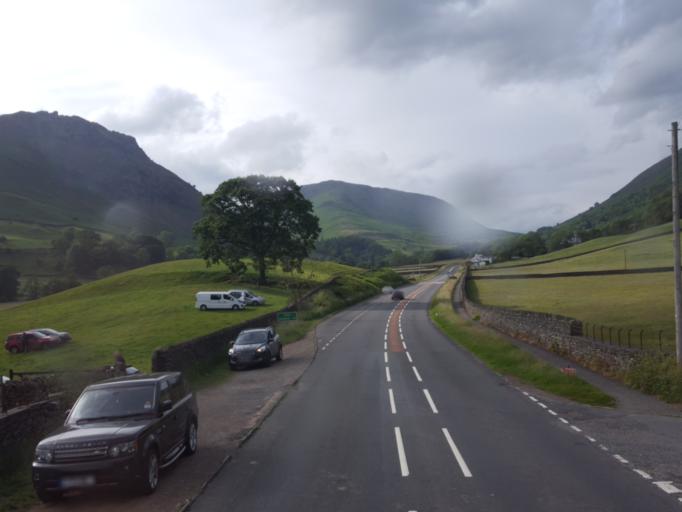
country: GB
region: England
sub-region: Cumbria
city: Ambleside
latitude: 54.4672
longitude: -3.0226
